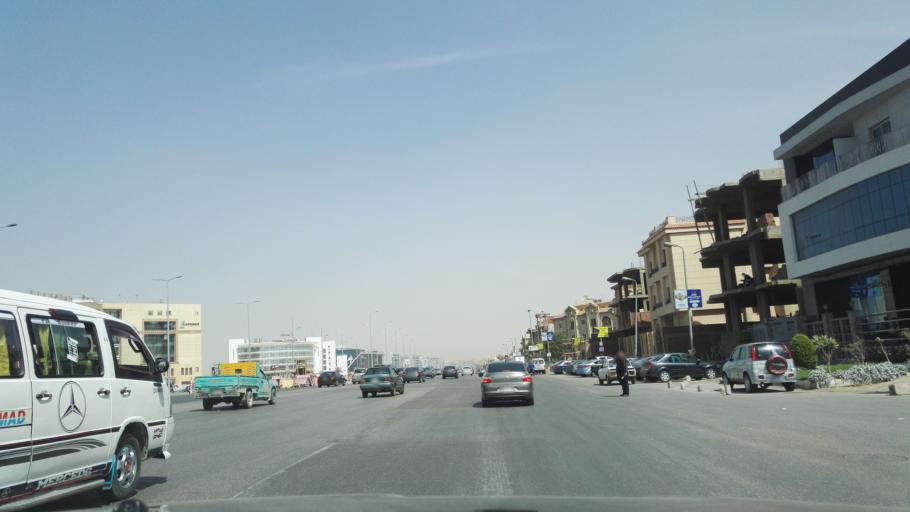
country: EG
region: Muhafazat al Qahirah
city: Cairo
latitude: 30.0160
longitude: 31.4118
